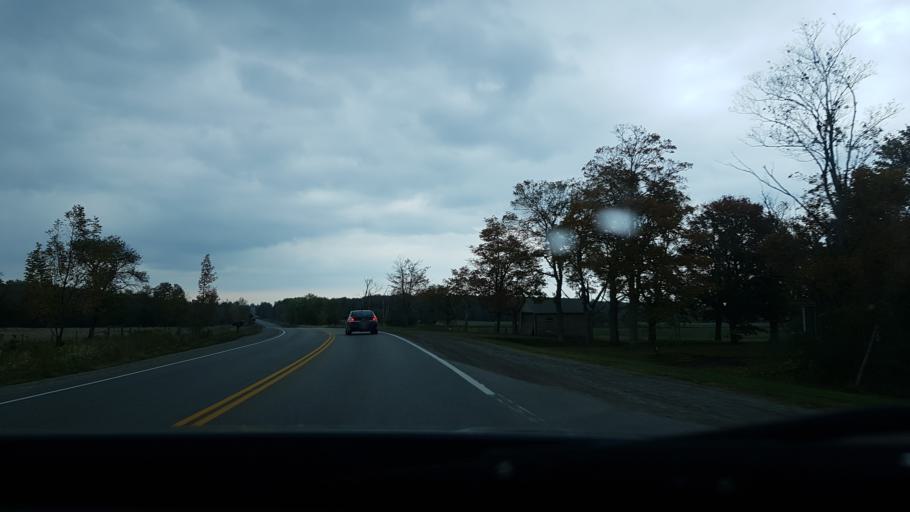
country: CA
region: Ontario
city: Omemee
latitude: 44.3754
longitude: -78.6369
